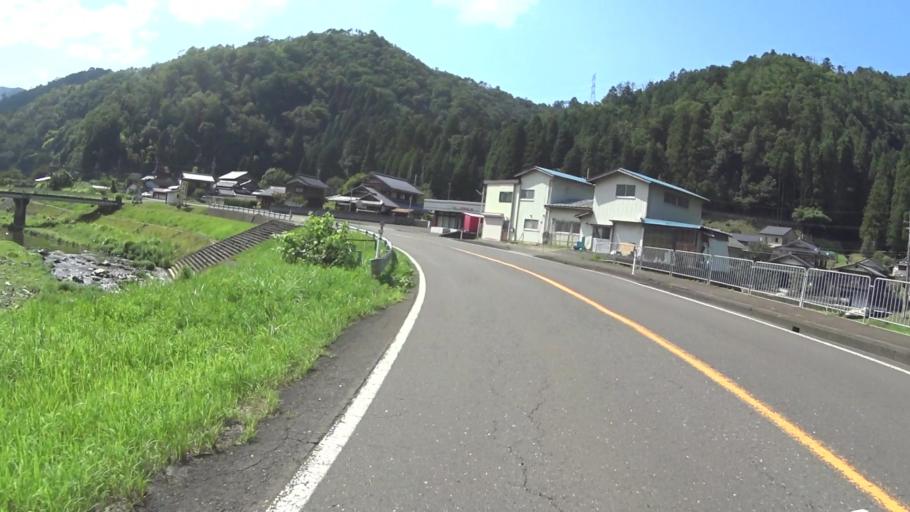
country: JP
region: Fukui
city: Obama
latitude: 35.3954
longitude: 135.5878
